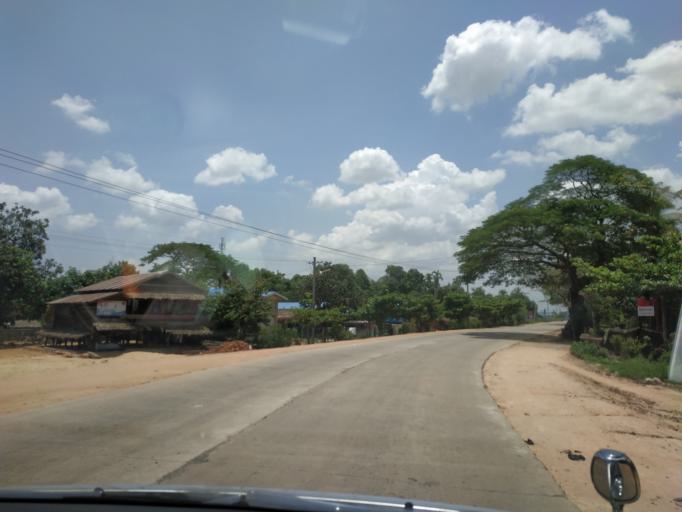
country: MM
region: Bago
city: Bago
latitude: 17.4798
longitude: 96.4868
